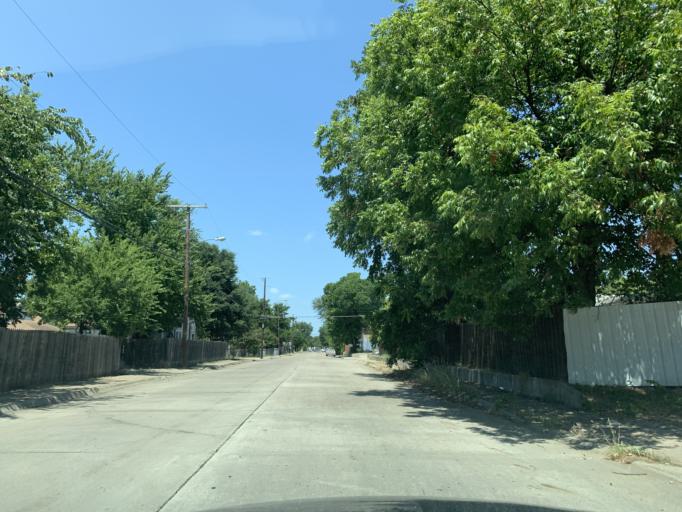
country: US
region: Texas
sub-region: Dallas County
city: Dallas
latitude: 32.6908
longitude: -96.8007
